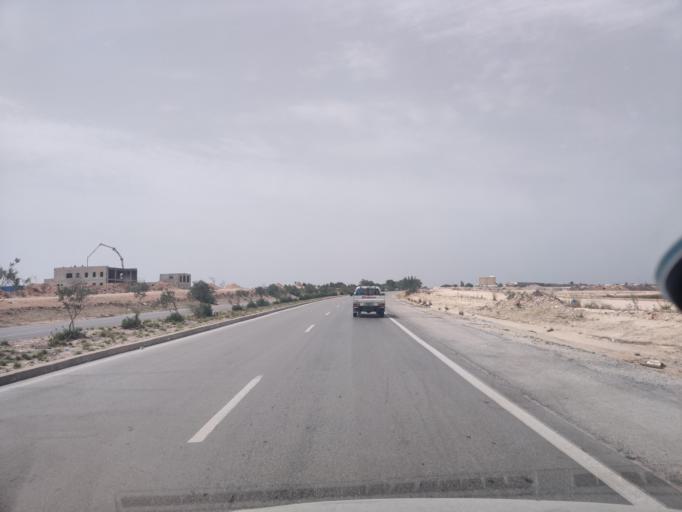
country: TN
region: Susah
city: Akouda
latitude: 35.8362
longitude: 10.5447
